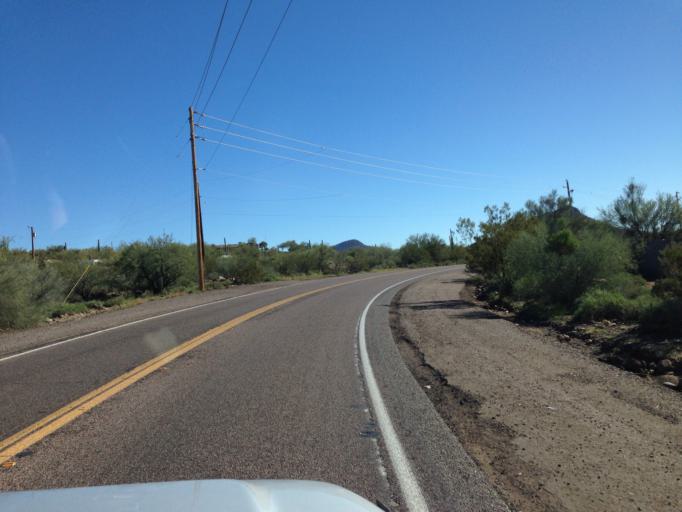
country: US
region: Arizona
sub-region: Maricopa County
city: New River
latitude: 33.9009
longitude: -112.0785
